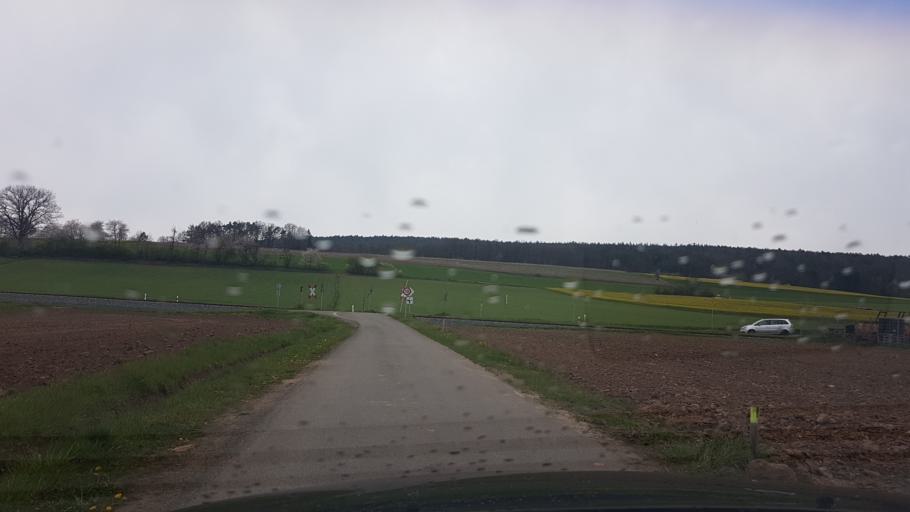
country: DE
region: Bavaria
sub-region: Upper Franconia
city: Reckendorf
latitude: 50.0388
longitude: 10.8312
